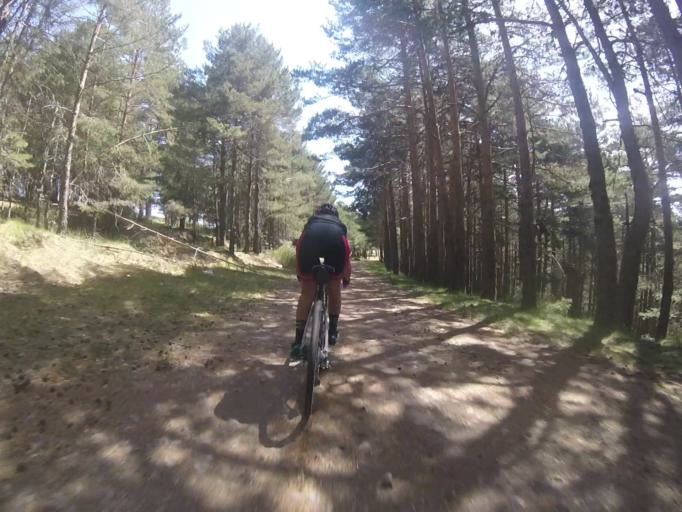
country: ES
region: Madrid
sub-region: Provincia de Madrid
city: Cercedilla
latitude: 40.8056
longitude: -4.0550
